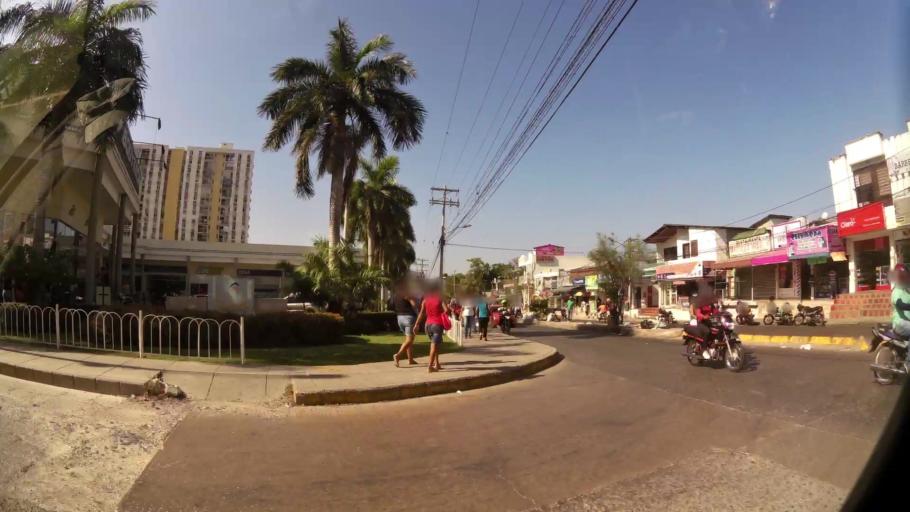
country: CO
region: Bolivar
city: Cartagena
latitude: 10.3905
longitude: -75.4799
